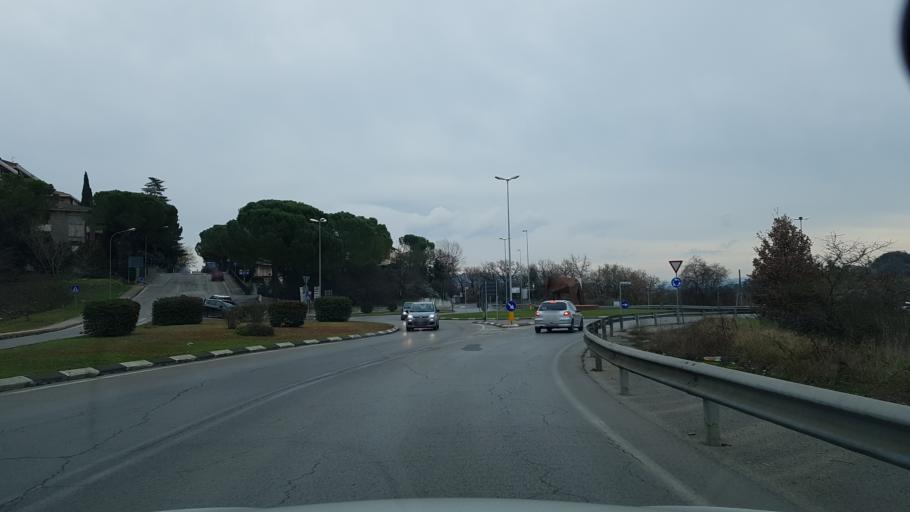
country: IT
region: Umbria
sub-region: Provincia di Perugia
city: Lacugnano
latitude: 43.1035
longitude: 12.3457
